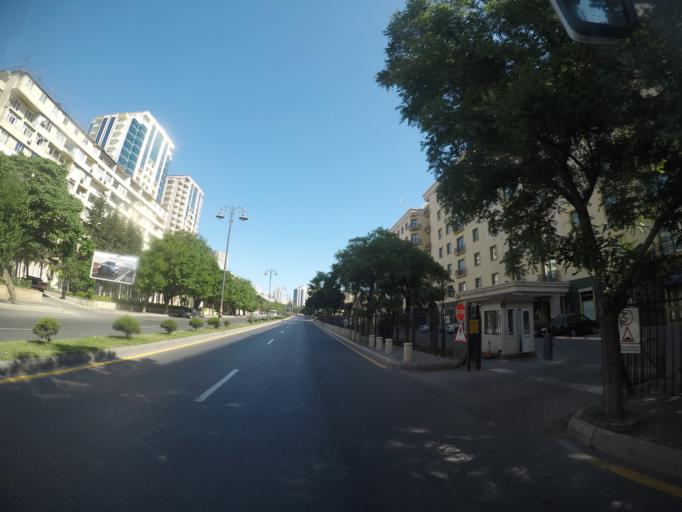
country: AZ
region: Baki
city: Badamdar
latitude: 40.3880
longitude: 49.8239
